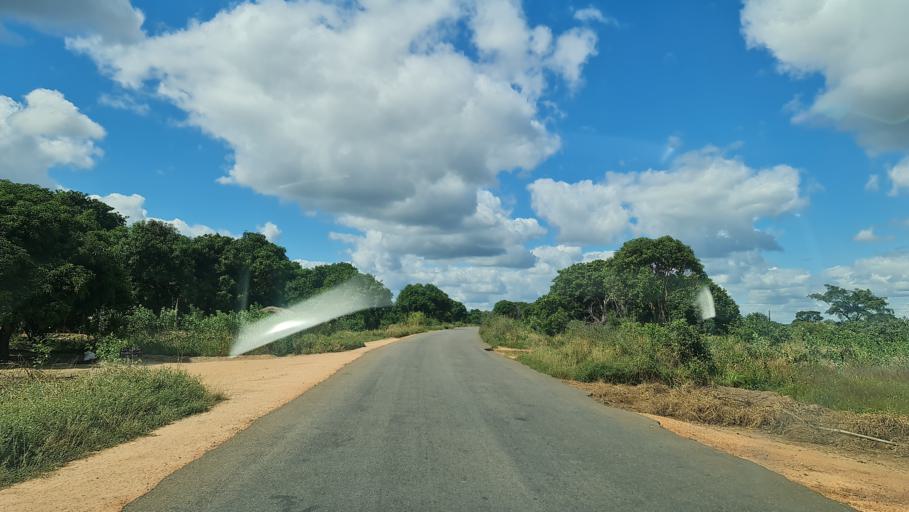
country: MZ
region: Zambezia
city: Quelimane
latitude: -17.5066
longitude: 36.2447
